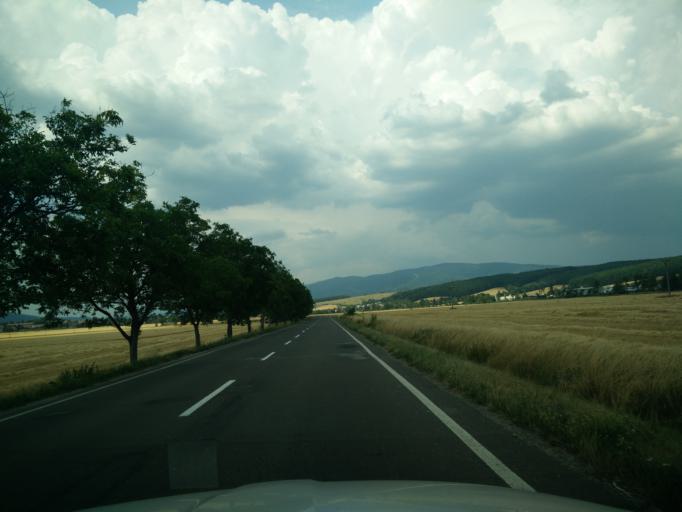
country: SK
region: Nitriansky
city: Novaky
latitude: 48.7541
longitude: 18.4976
